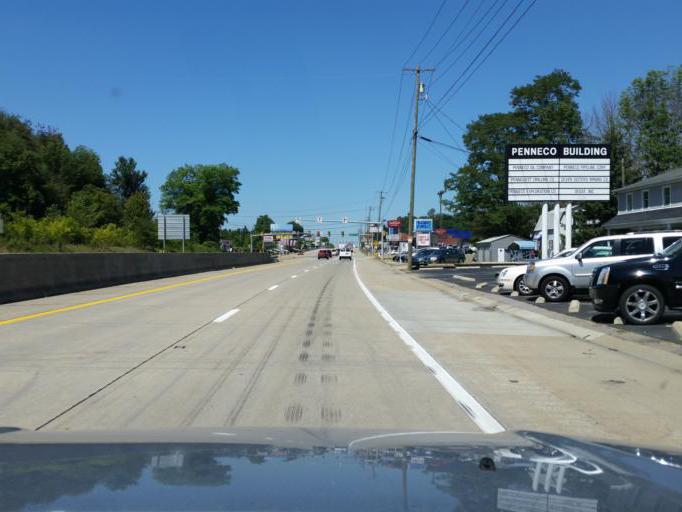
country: US
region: Pennsylvania
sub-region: Westmoreland County
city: Delmont
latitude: 40.3987
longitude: -79.5776
